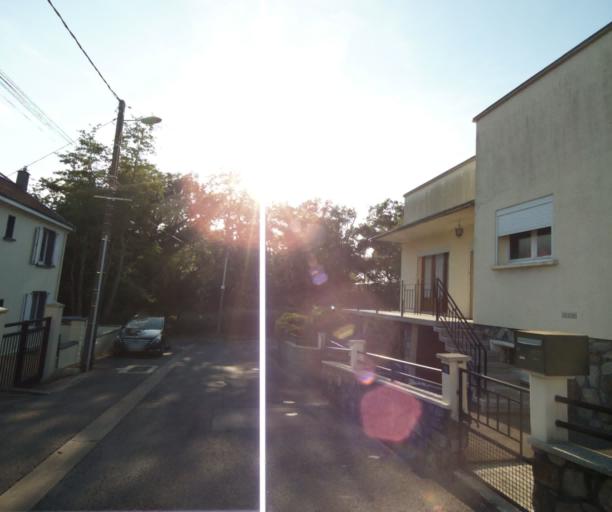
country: FR
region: Champagne-Ardenne
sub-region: Departement des Ardennes
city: Charleville-Mezieres
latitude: 49.7860
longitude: 4.7084
